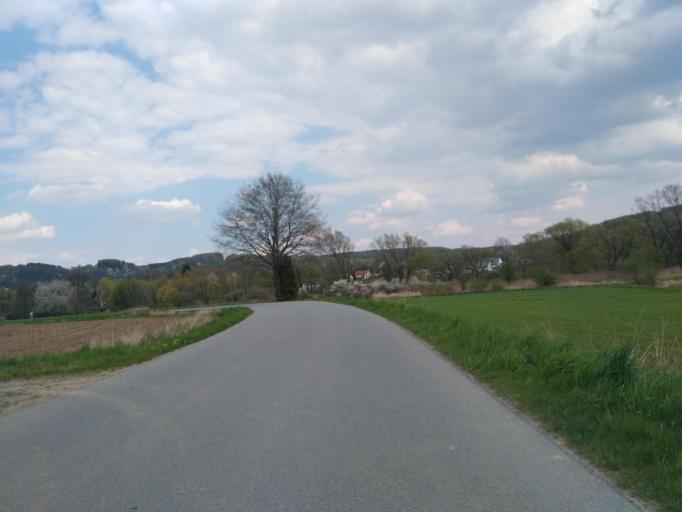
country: PL
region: Subcarpathian Voivodeship
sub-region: Powiat krosnienski
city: Wojaszowka
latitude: 49.7821
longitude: 21.6784
